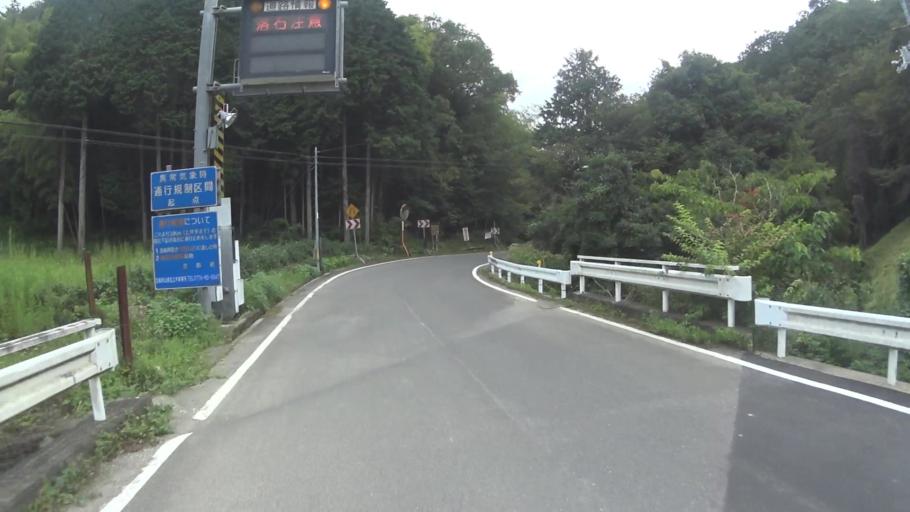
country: JP
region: Kyoto
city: Tanabe
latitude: 34.8077
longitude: 135.8515
